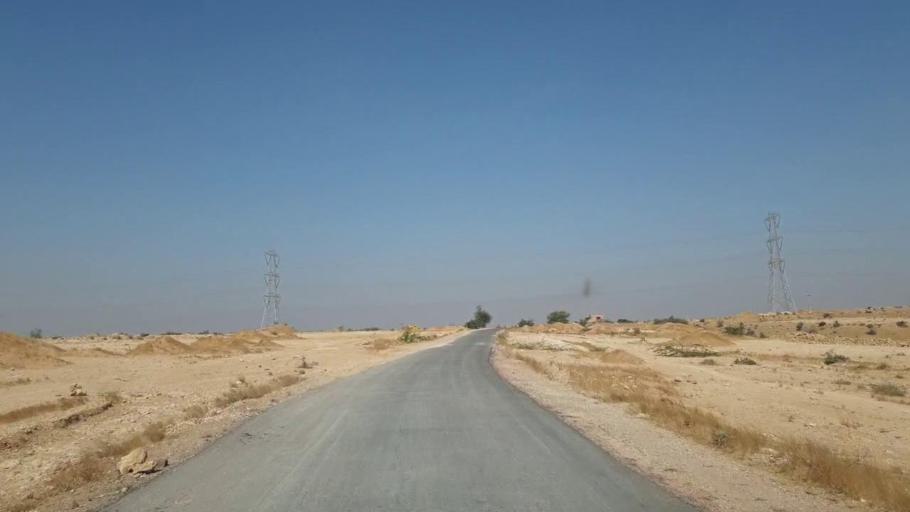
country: PK
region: Sindh
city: Thatta
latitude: 25.1998
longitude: 67.7978
